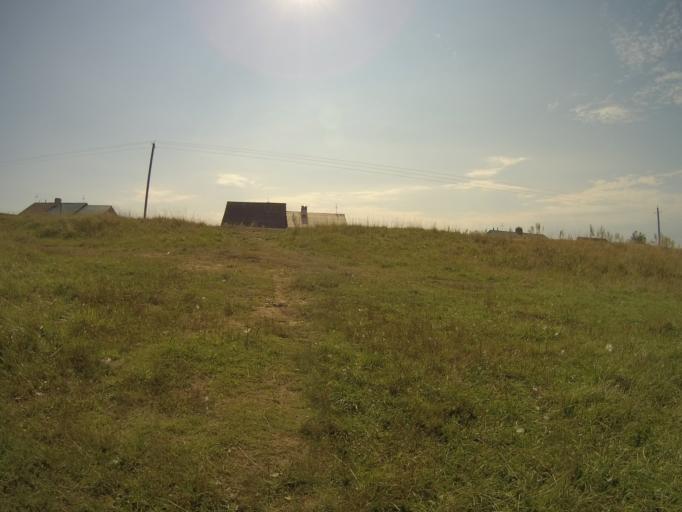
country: RU
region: Vladimir
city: Orgtrud
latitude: 56.0393
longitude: 40.6844
